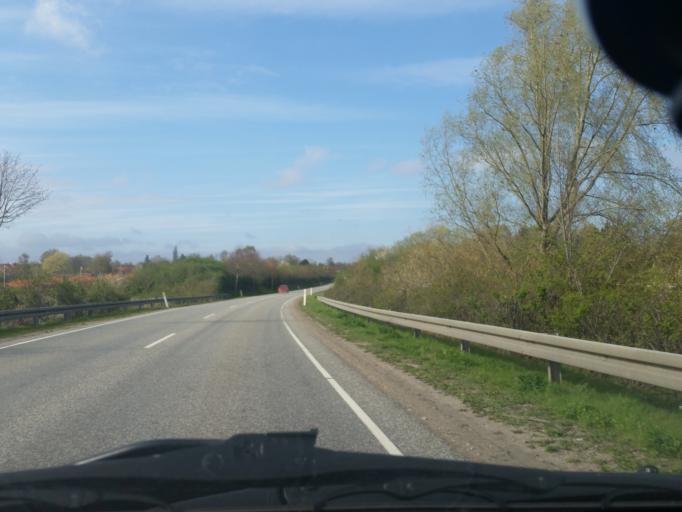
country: DK
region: Zealand
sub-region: Soro Kommune
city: Soro
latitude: 55.4490
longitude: 11.5619
